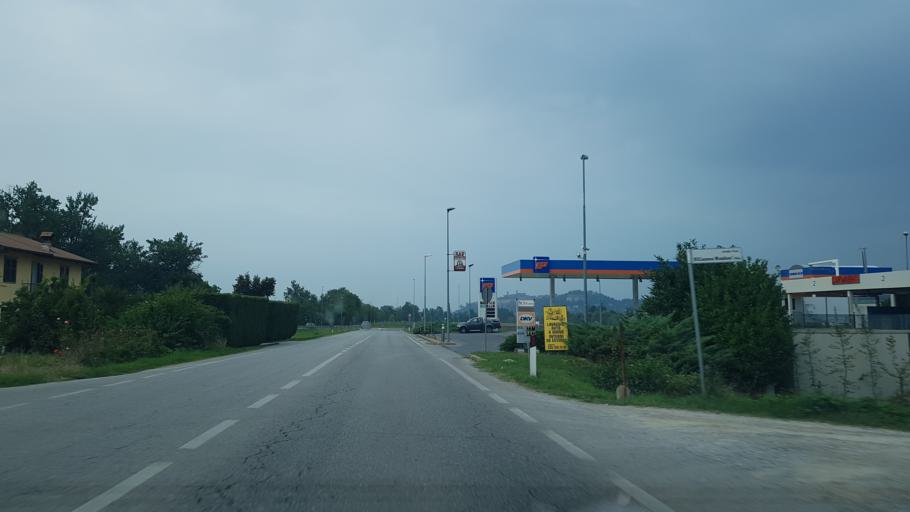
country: IT
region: Piedmont
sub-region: Provincia di Cuneo
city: Villanova Mondovi
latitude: 44.3660
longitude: 7.7966
